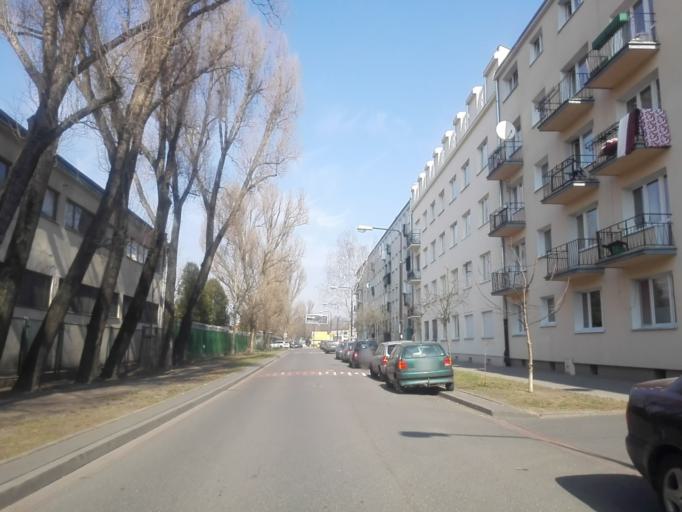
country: PL
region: Masovian Voivodeship
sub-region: Warszawa
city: Mokotow
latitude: 52.2116
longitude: 21.0455
